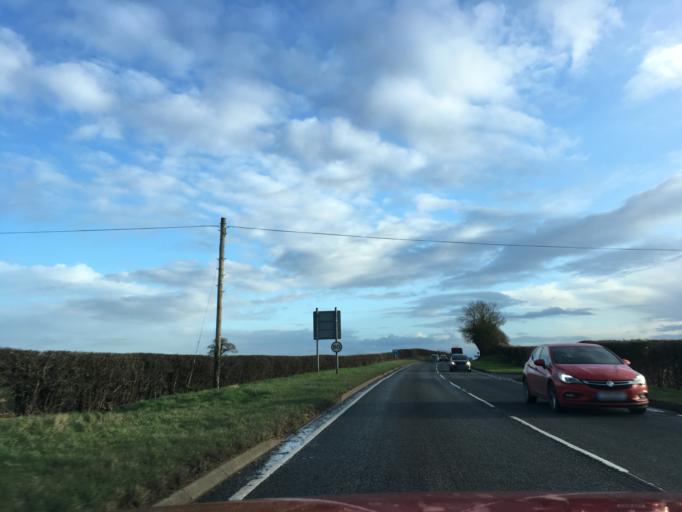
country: GB
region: England
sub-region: Warwickshire
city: Stratford-upon-Avon
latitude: 52.2224
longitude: -1.7348
